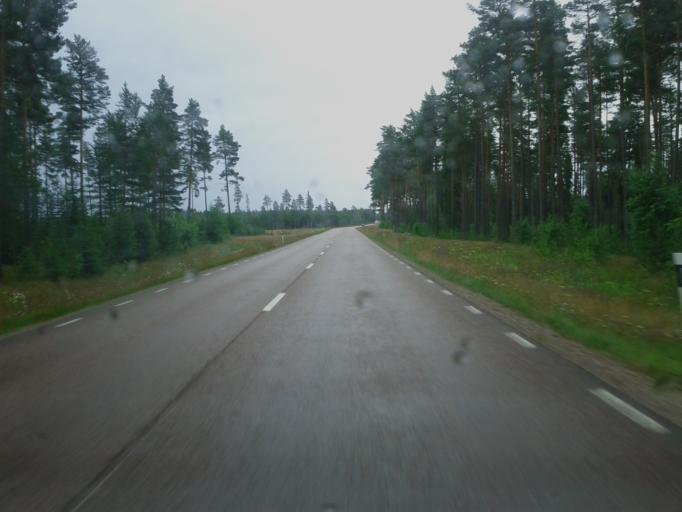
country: SE
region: Dalarna
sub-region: Mora Kommun
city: Mora
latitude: 60.9810
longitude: 14.6900
